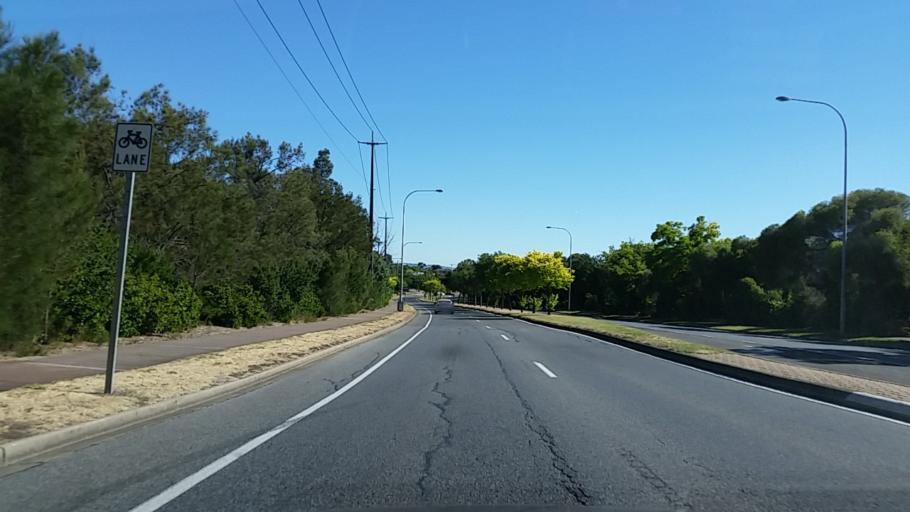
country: AU
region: South Australia
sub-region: Tea Tree Gully
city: Modbury
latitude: -34.8004
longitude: 138.6853
